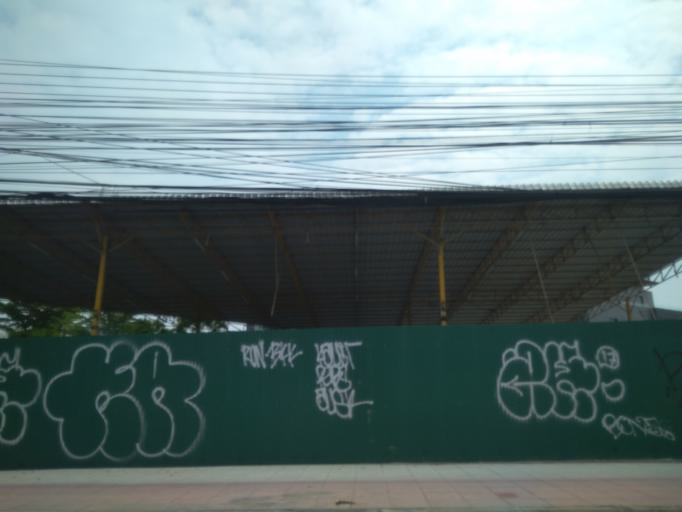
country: TH
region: Bangkok
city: Suan Luang
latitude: 13.7321
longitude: 100.6414
